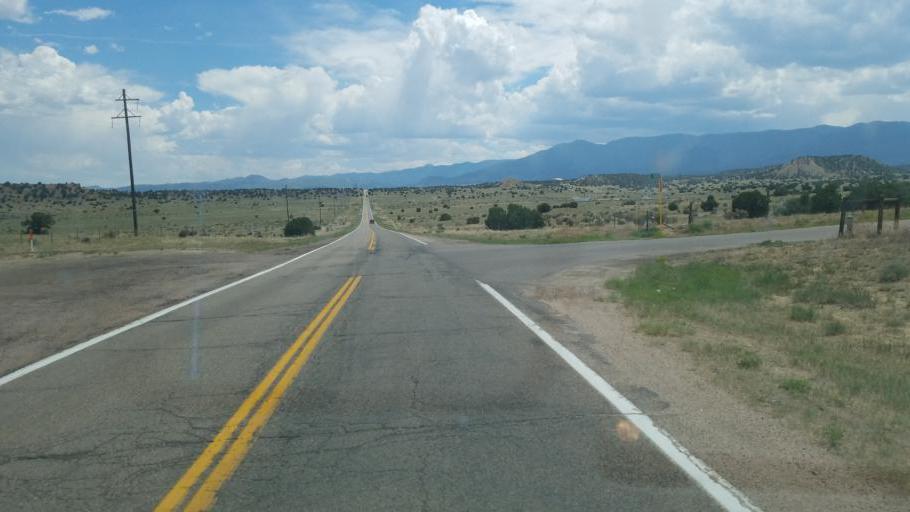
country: US
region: Colorado
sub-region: Fremont County
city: Florence
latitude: 38.3455
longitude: -105.1071
